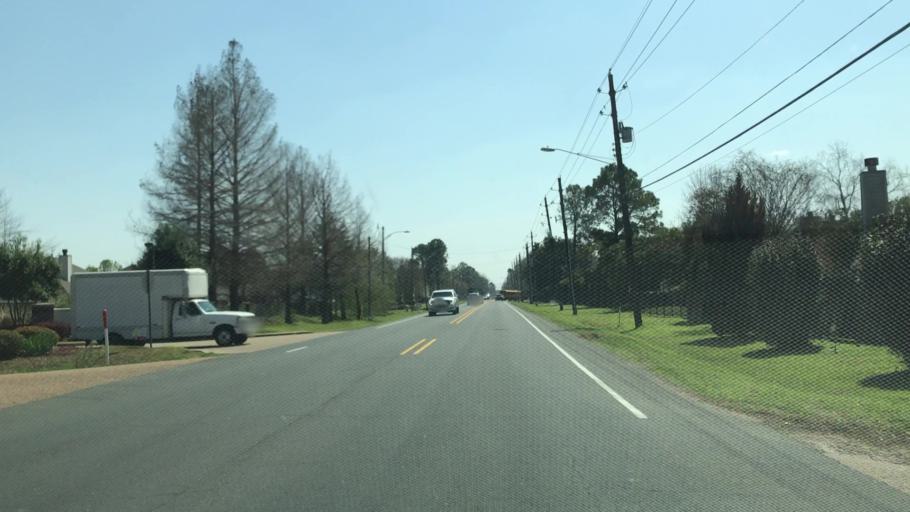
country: US
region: Louisiana
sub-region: Bossier Parish
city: Bossier City
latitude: 32.4177
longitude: -93.6934
